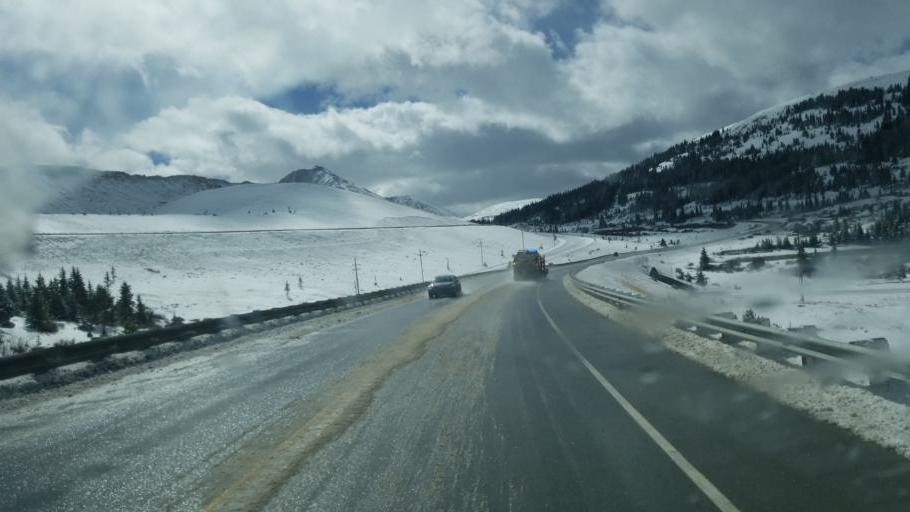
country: US
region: Colorado
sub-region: Lake County
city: Leadville
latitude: 39.3827
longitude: -106.1906
